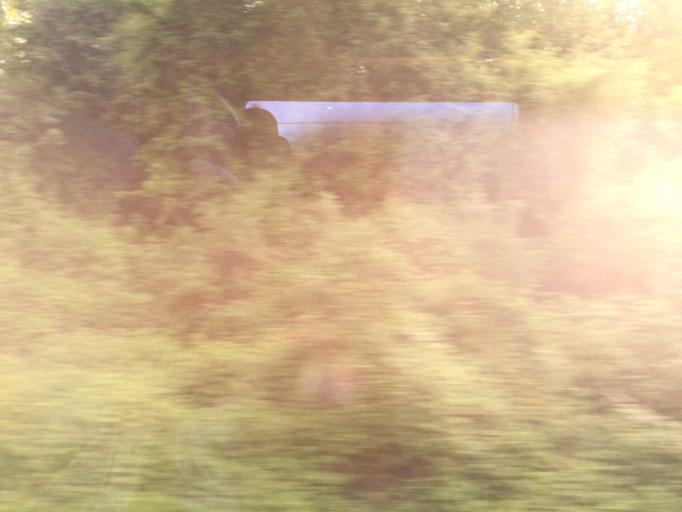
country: DE
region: North Rhine-Westphalia
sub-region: Regierungsbezirk Dusseldorf
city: Muelheim (Ruhr)
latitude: 51.4435
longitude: 6.8672
